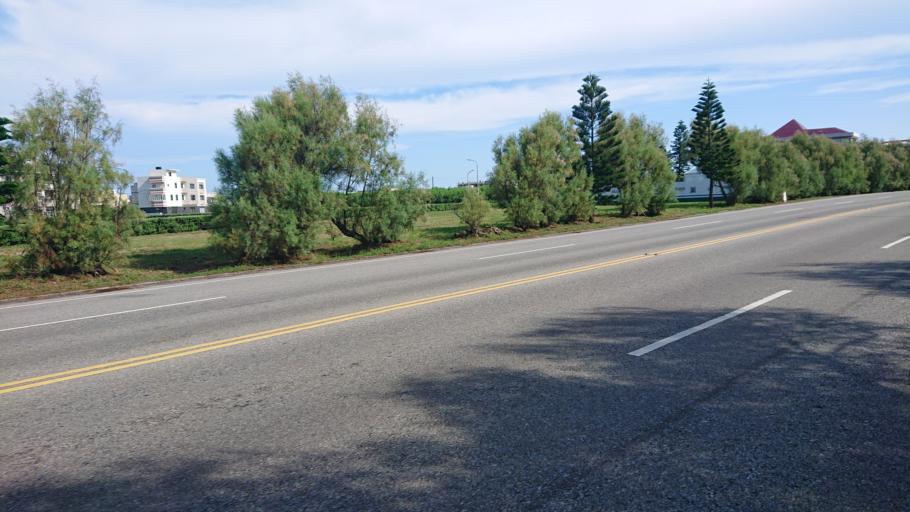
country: TW
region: Taiwan
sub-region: Penghu
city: Ma-kung
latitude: 23.5300
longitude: 119.5999
